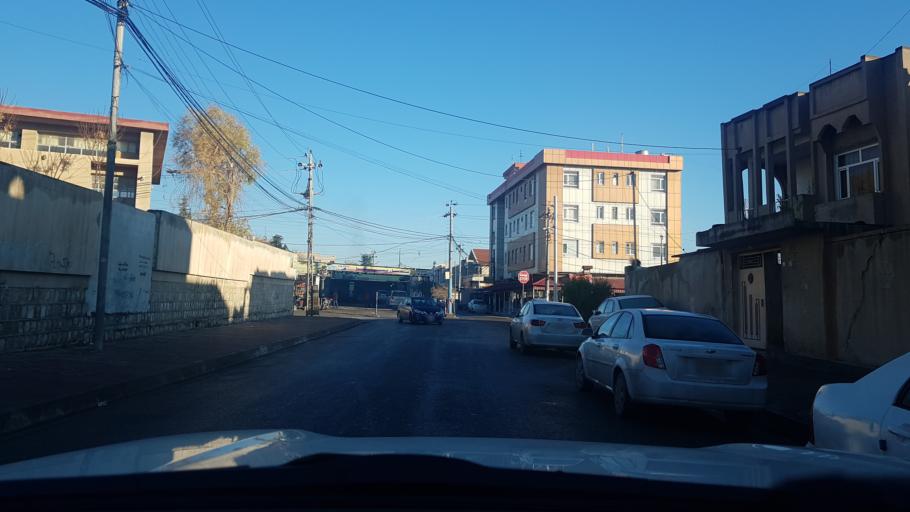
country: IQ
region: Arbil
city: Erbil
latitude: 36.2062
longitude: 44.0088
